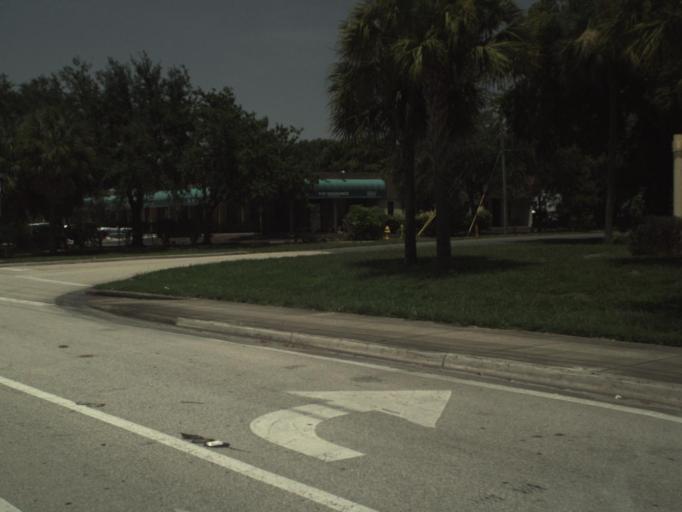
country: US
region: Florida
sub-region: Broward County
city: Kendall Green
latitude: 26.2617
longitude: -80.1518
